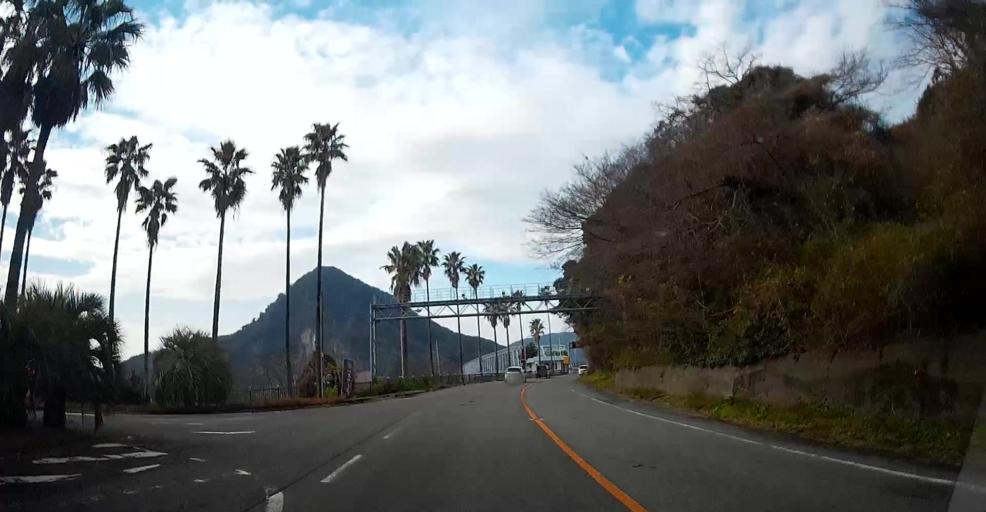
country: JP
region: Kumamoto
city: Yatsushiro
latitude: 32.6093
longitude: 130.4630
